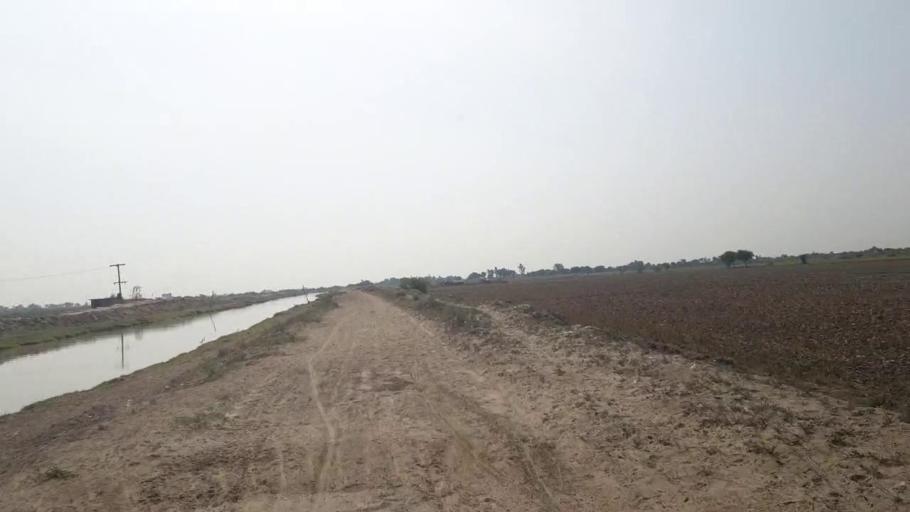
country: PK
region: Sindh
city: Badin
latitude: 24.5501
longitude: 68.8499
